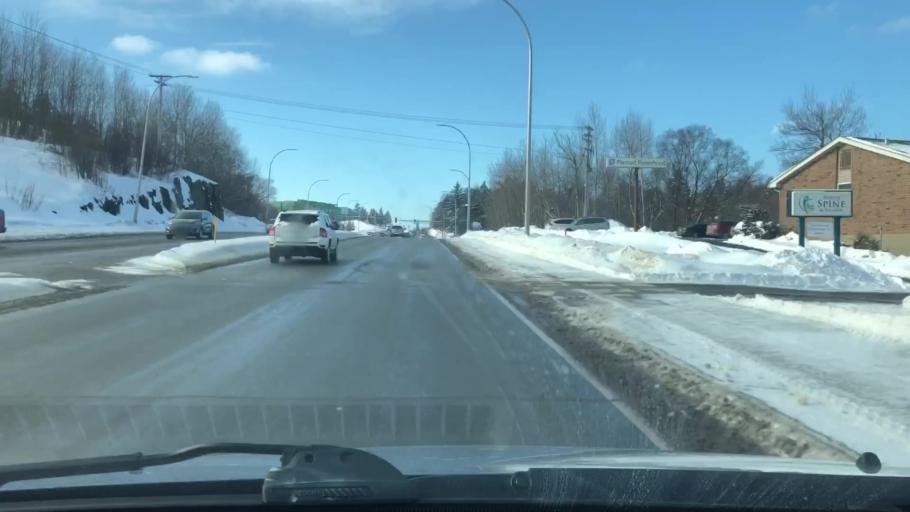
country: US
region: Minnesota
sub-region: Saint Louis County
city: Duluth
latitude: 46.7992
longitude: -92.1128
